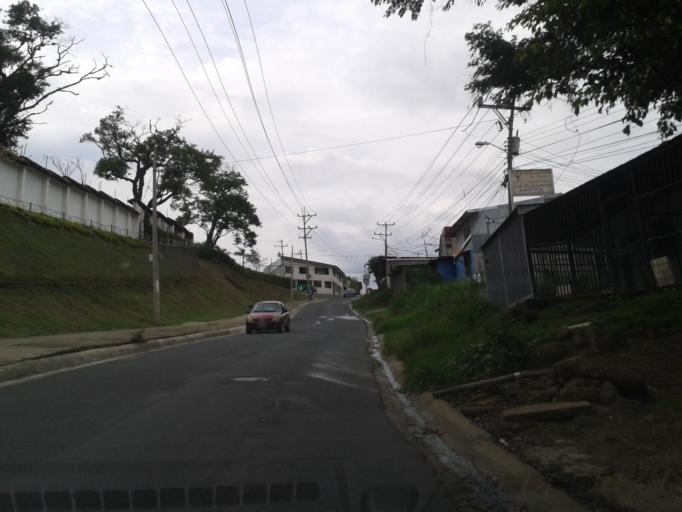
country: CR
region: Heredia
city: San Francisco
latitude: 9.9846
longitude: -84.1211
